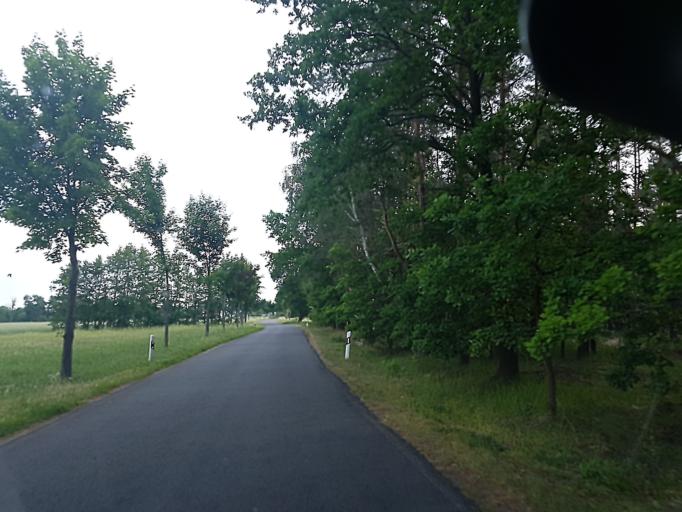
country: DE
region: Saxony-Anhalt
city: Holzdorf
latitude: 51.7733
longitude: 13.1116
